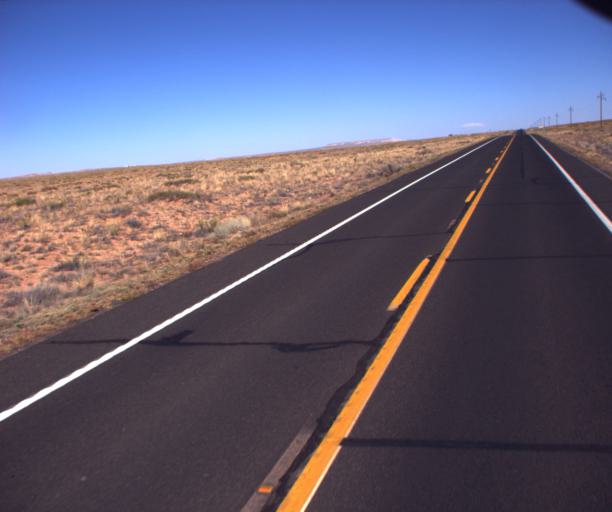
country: US
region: Arizona
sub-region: Coconino County
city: Tuba City
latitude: 36.1398
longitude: -111.1636
